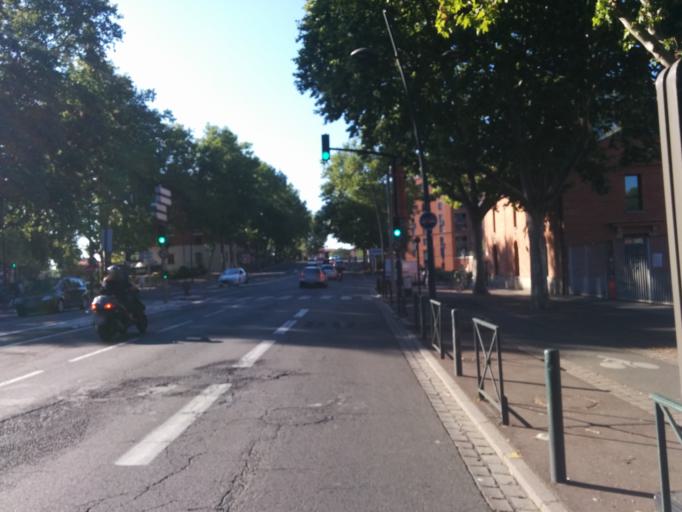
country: FR
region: Midi-Pyrenees
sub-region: Departement de la Haute-Garonne
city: Toulouse
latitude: 43.6005
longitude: 1.4289
